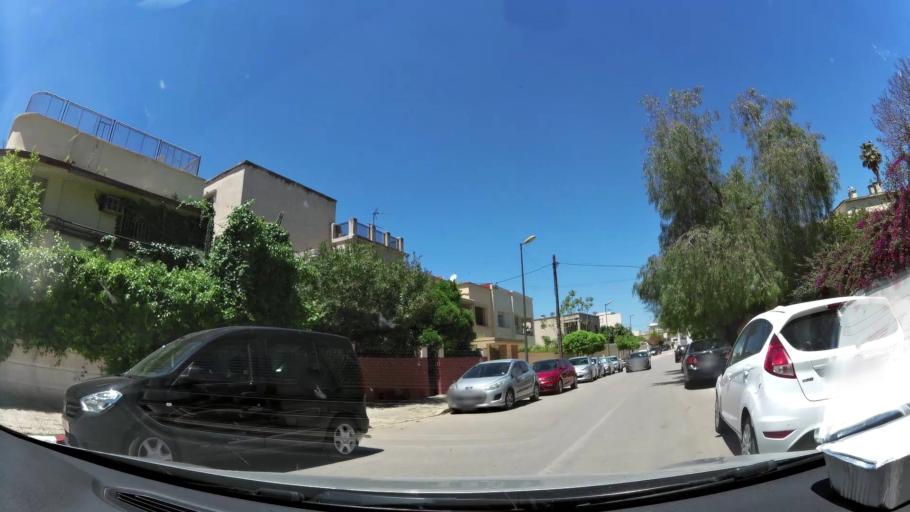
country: MA
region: Meknes-Tafilalet
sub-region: Meknes
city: Meknes
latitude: 33.9021
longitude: -5.5531
